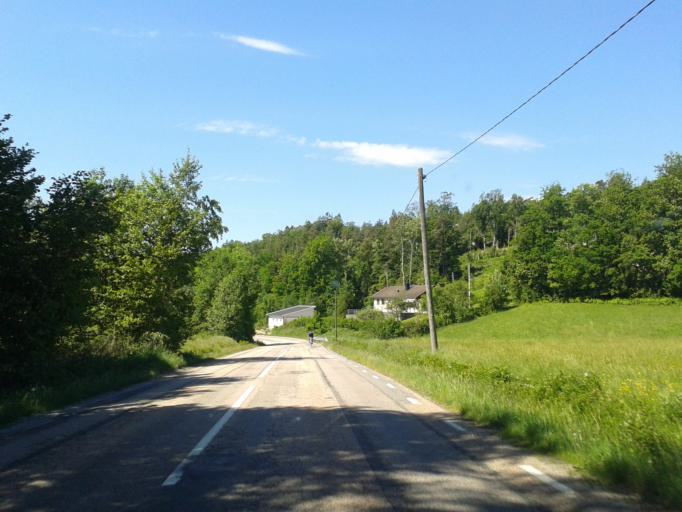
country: SE
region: Vaestra Goetaland
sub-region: Orust
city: Henan
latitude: 58.2858
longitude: 11.7085
